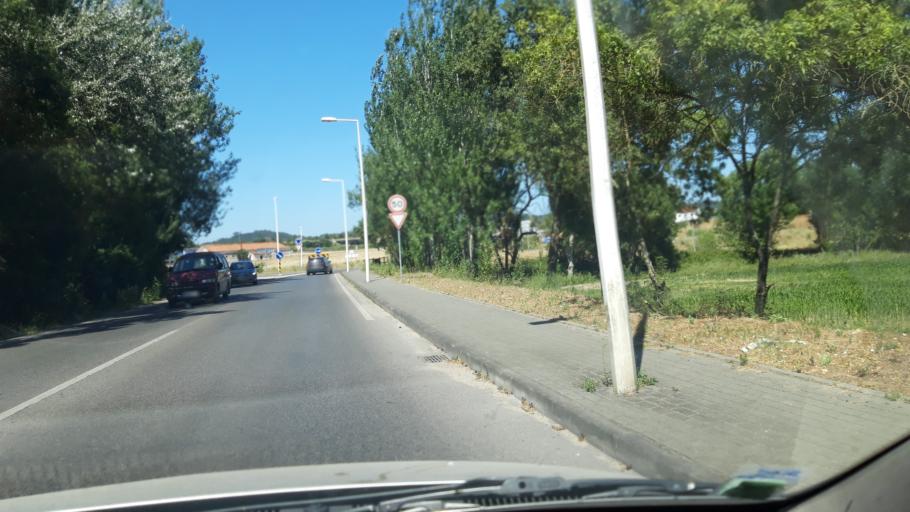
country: PT
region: Santarem
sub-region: Entroncamento
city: Entroncamento
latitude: 39.4640
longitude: -8.4613
